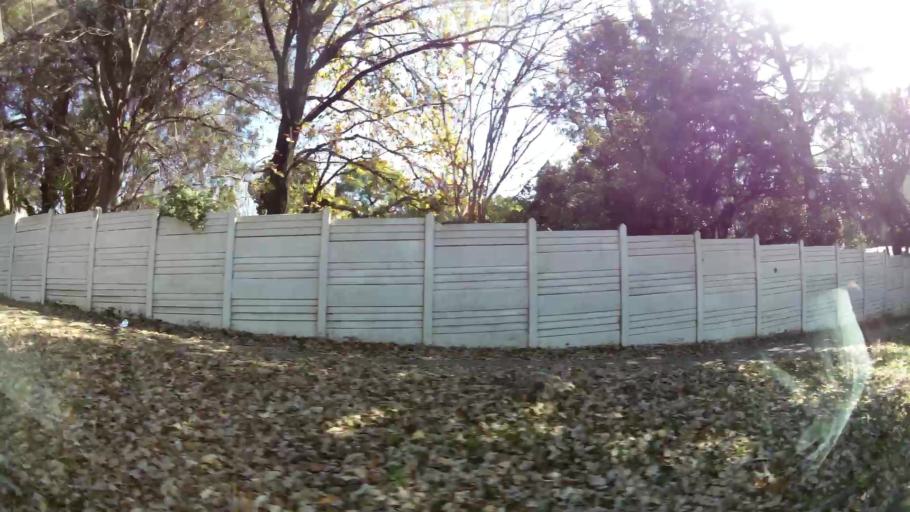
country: ZA
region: Gauteng
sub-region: City of Johannesburg Metropolitan Municipality
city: Modderfontein
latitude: -26.1595
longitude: 28.1235
